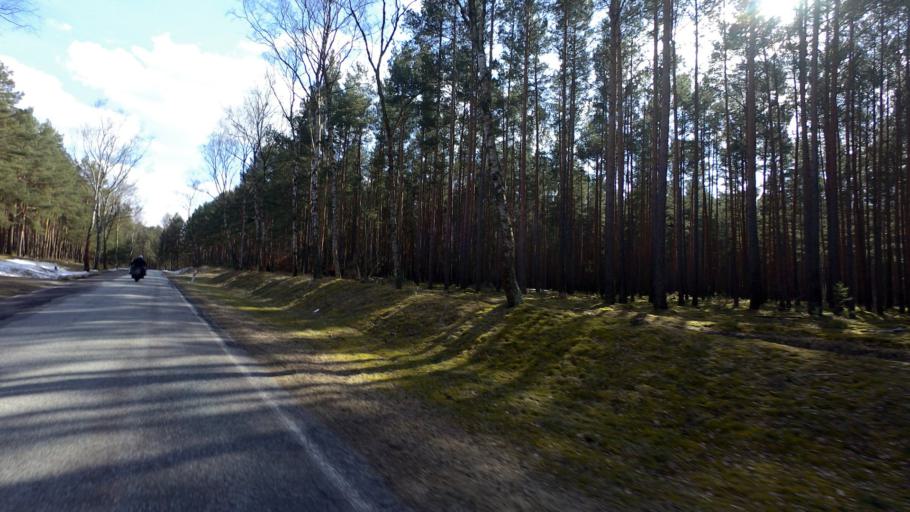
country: DE
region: Brandenburg
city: Biesenthal
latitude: 52.7810
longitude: 13.6125
